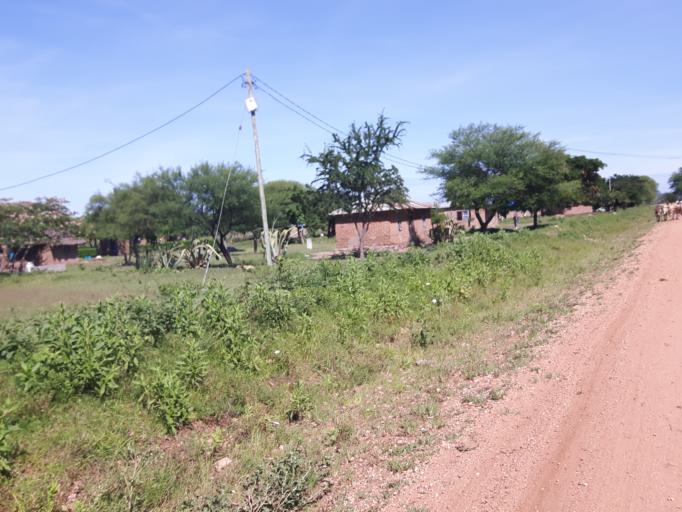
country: TZ
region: Mara
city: Issenye
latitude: -1.9613
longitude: 34.2720
